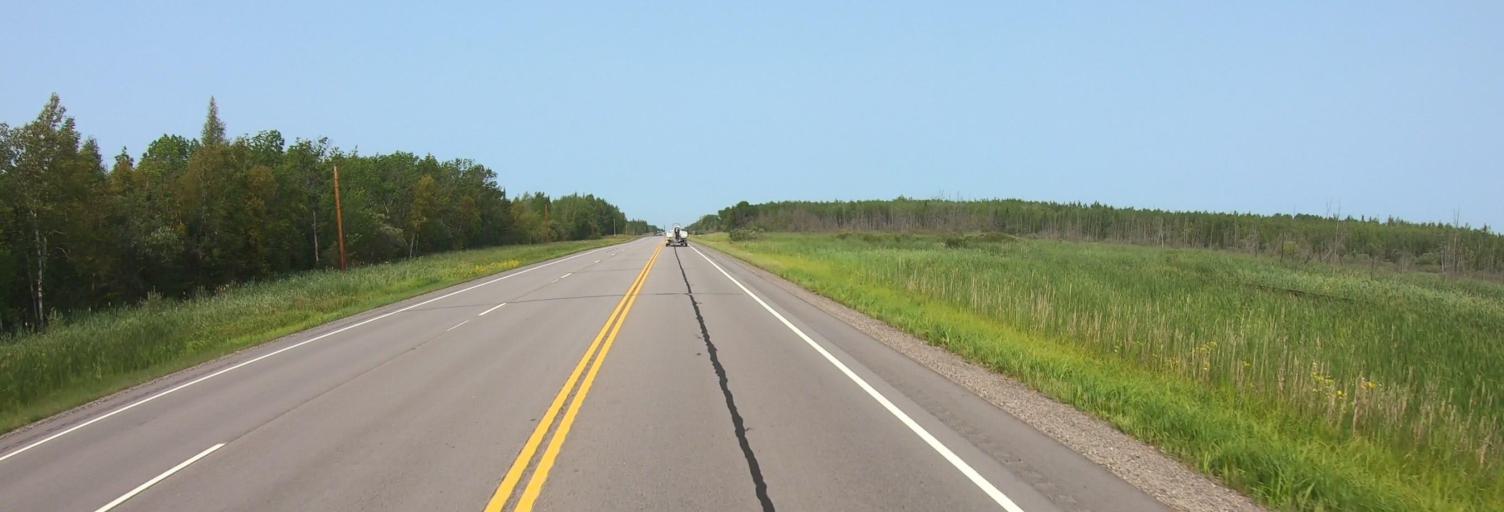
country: CA
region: Ontario
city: Fort Frances
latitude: 48.4390
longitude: -93.2532
